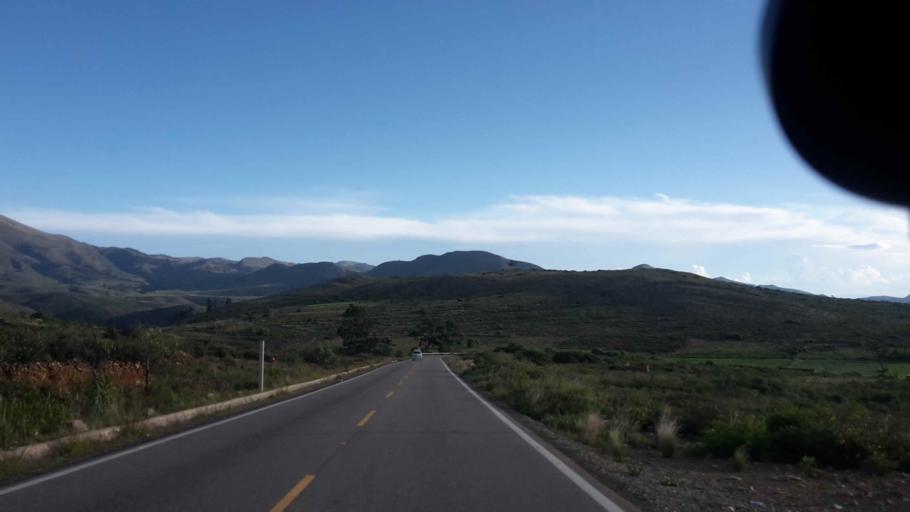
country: BO
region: Cochabamba
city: Arani
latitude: -17.5793
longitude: -65.7389
